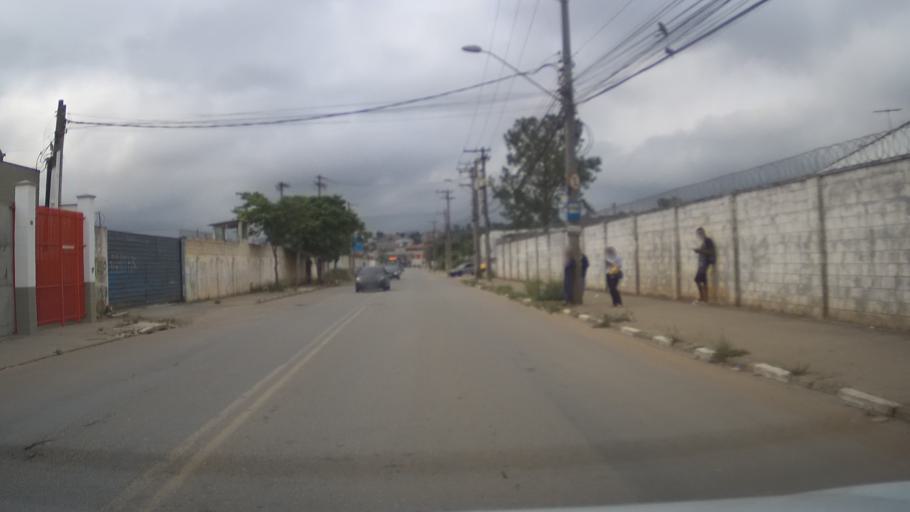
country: BR
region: Sao Paulo
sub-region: Aruja
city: Aruja
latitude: -23.4169
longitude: -46.3833
